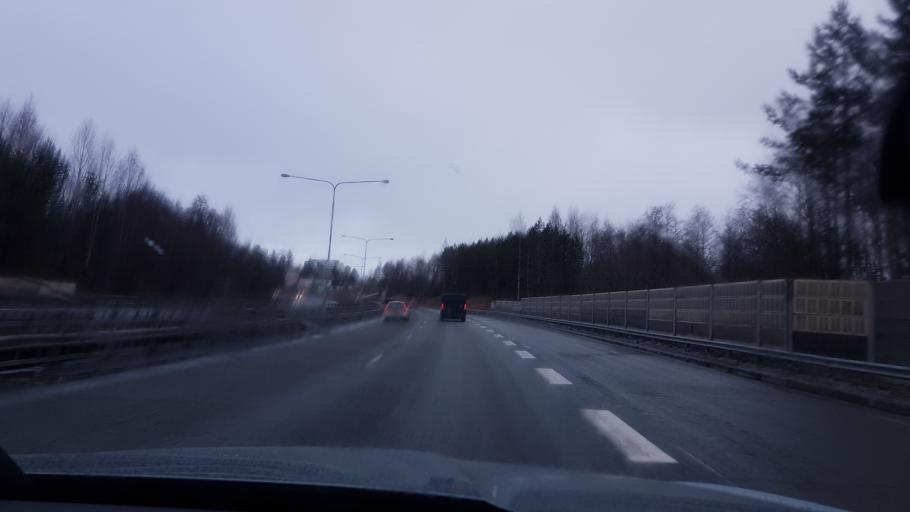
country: FI
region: Pirkanmaa
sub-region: Tampere
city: Tampere
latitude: 61.4698
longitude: 23.8540
